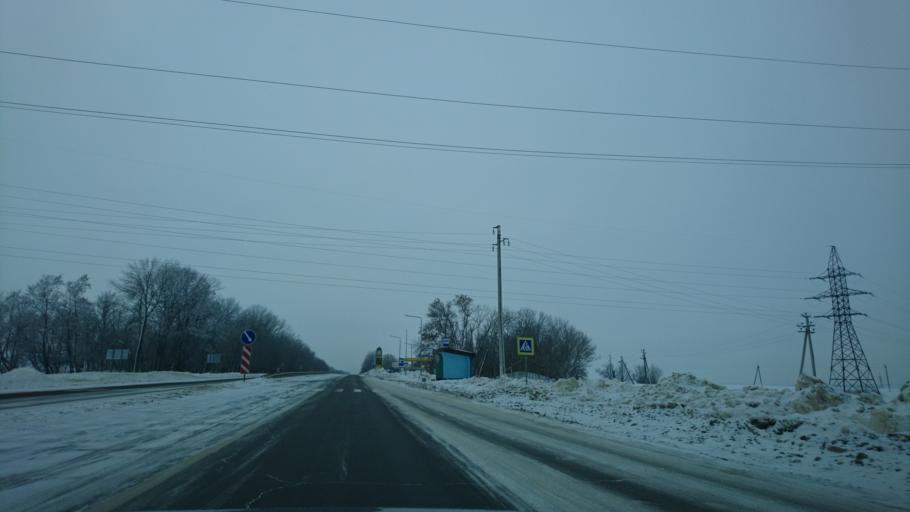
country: RU
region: Belgorod
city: Mayskiy
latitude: 50.4368
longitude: 36.3906
